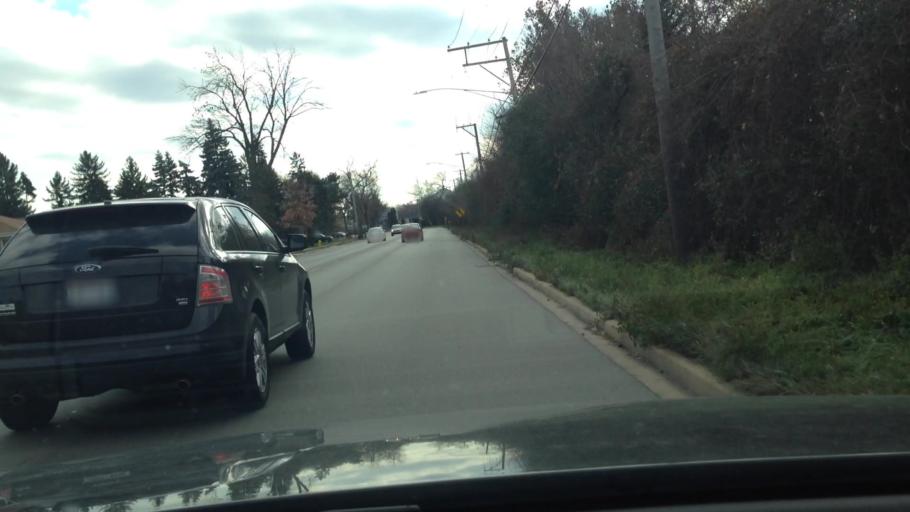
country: US
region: Illinois
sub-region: Cook County
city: Harwood Heights
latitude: 41.9668
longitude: -87.7881
